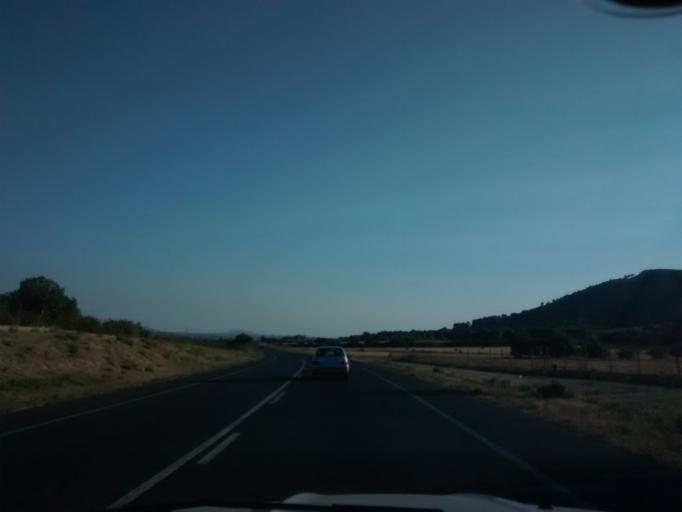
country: ES
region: Balearic Islands
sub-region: Illes Balears
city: Alcudia
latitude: 39.8281
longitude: 3.0616
